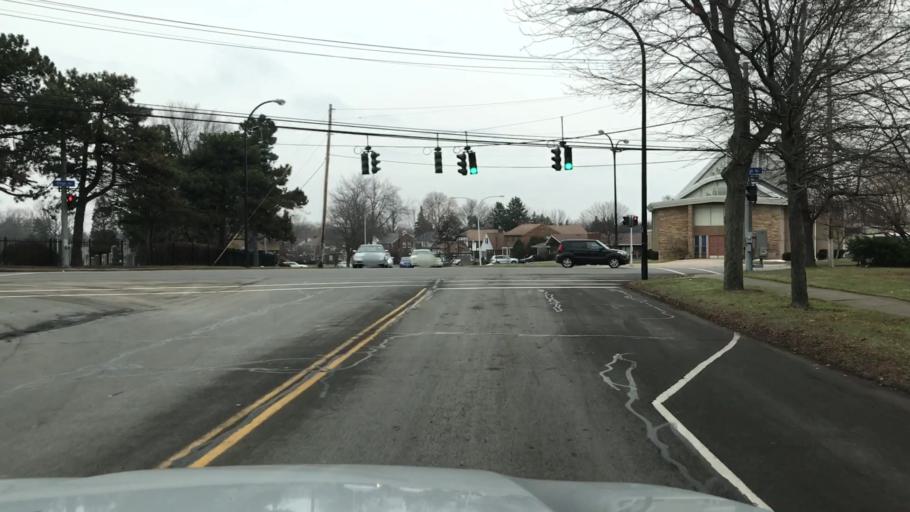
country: US
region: New York
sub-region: Erie County
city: Lackawanna
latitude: 42.8280
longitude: -78.8096
